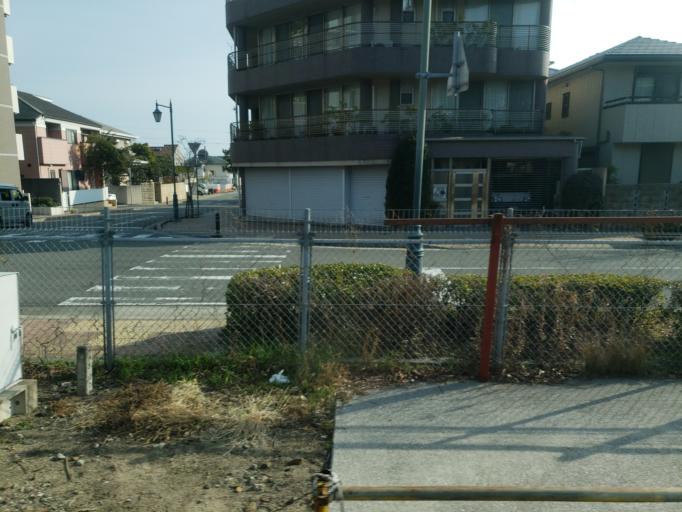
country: JP
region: Hyogo
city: Ashiya
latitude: 34.7316
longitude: 135.2969
